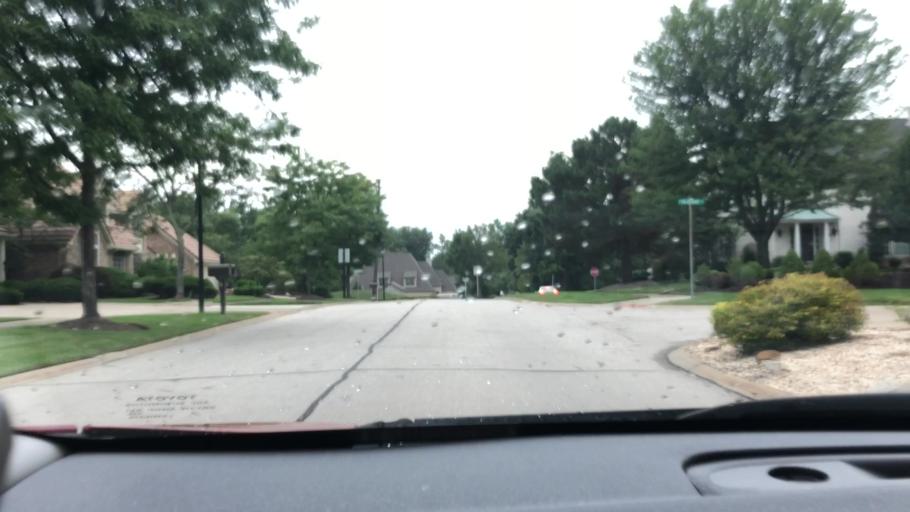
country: US
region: Ohio
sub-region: Cuyahoga County
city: Fairview Park
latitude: 41.4556
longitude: -81.8776
